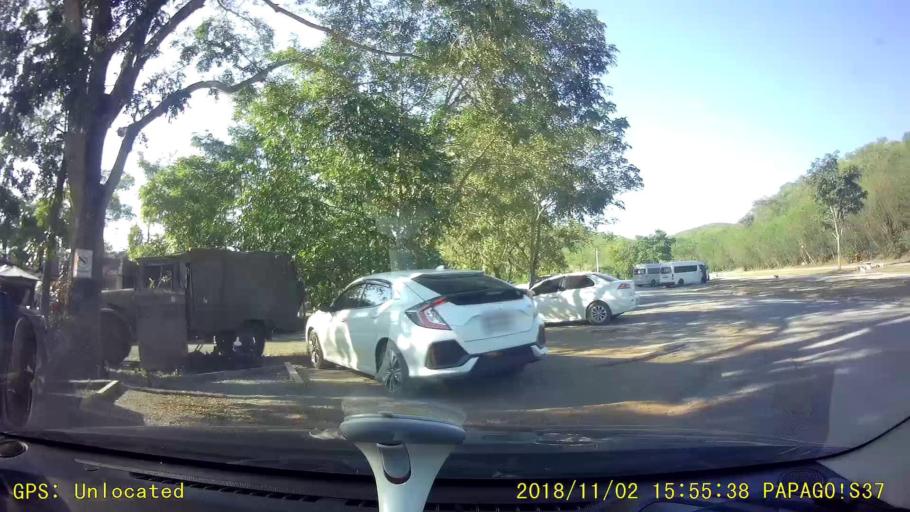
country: TH
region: Nakhon Ratchasima
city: Pak Chong
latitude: 14.7291
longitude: 101.3923
